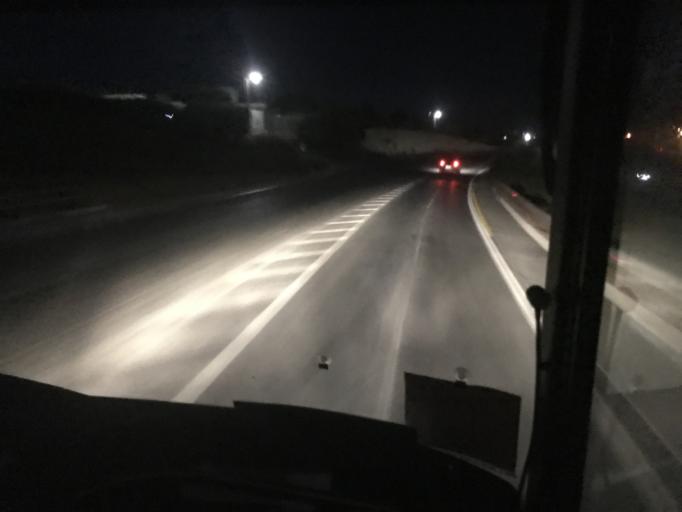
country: GR
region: Crete
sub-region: Nomos Irakleiou
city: Skalanion
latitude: 35.2621
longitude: 25.1816
